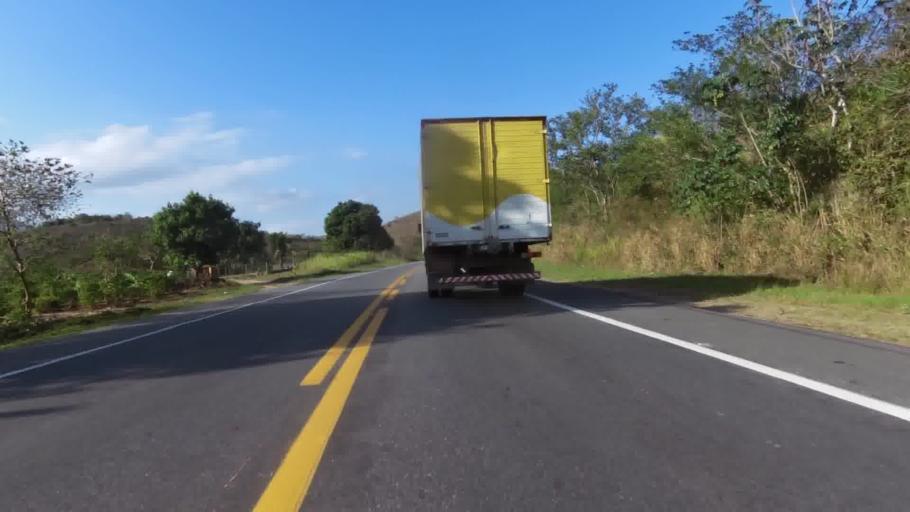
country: BR
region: Espirito Santo
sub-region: Mimoso Do Sul
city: Mimoso do Sul
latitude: -21.1695
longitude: -41.2903
